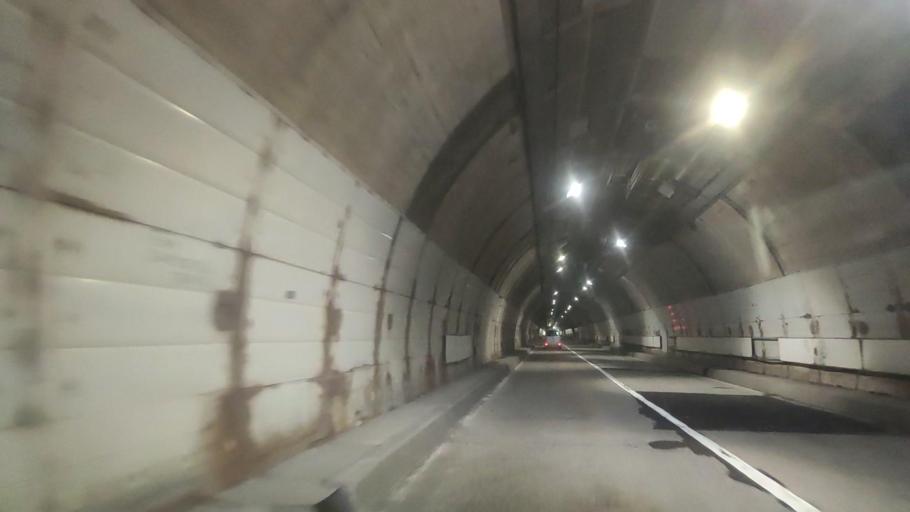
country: JP
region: Hokkaido
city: Niseko Town
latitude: 42.6009
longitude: 140.4746
